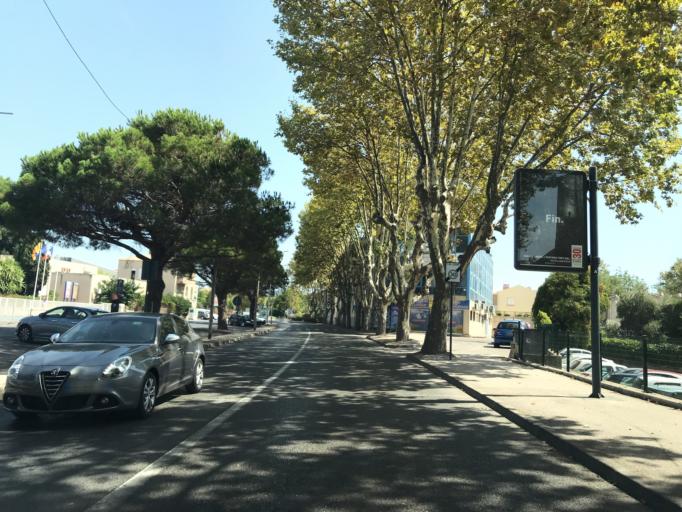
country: FR
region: Provence-Alpes-Cote d'Azur
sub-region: Departement du Var
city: Six-Fours-les-Plages
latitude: 43.0933
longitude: 5.8419
